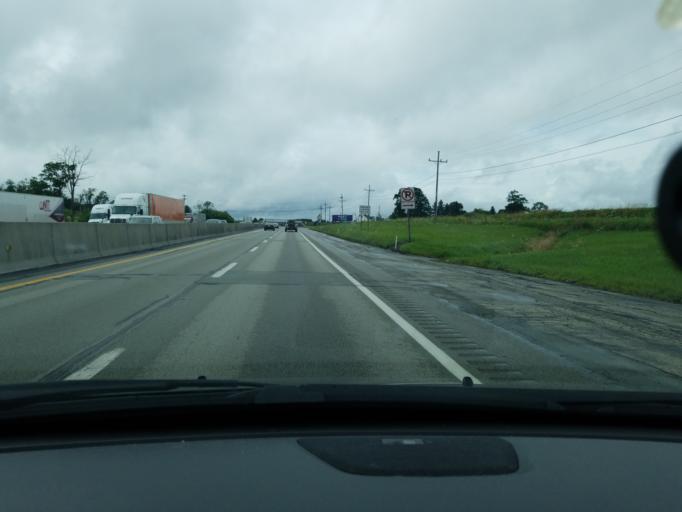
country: US
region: Pennsylvania
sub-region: Somerset County
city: Somerset
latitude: 40.0348
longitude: -79.0979
